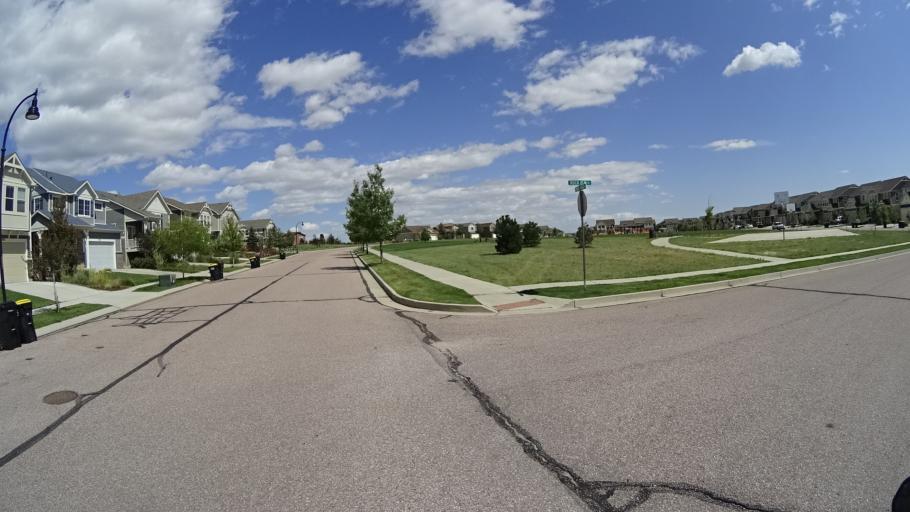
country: US
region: Colorado
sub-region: El Paso County
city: Cimarron Hills
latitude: 38.9282
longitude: -104.6743
